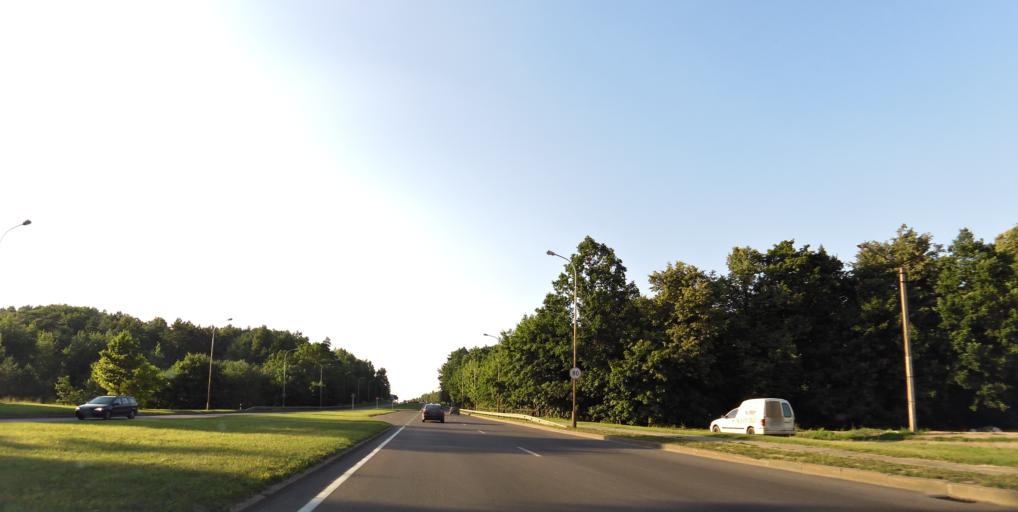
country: LT
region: Vilnius County
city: Seskine
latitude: 54.7231
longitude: 25.2699
